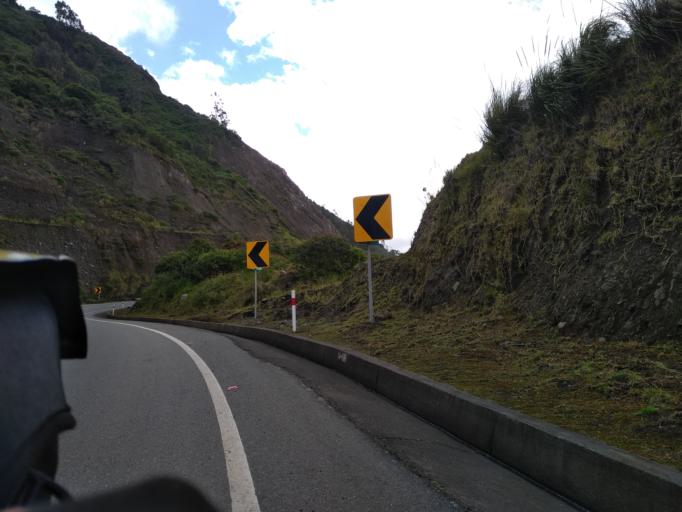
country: EC
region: Tungurahua
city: Banos
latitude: -1.4754
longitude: -78.5172
